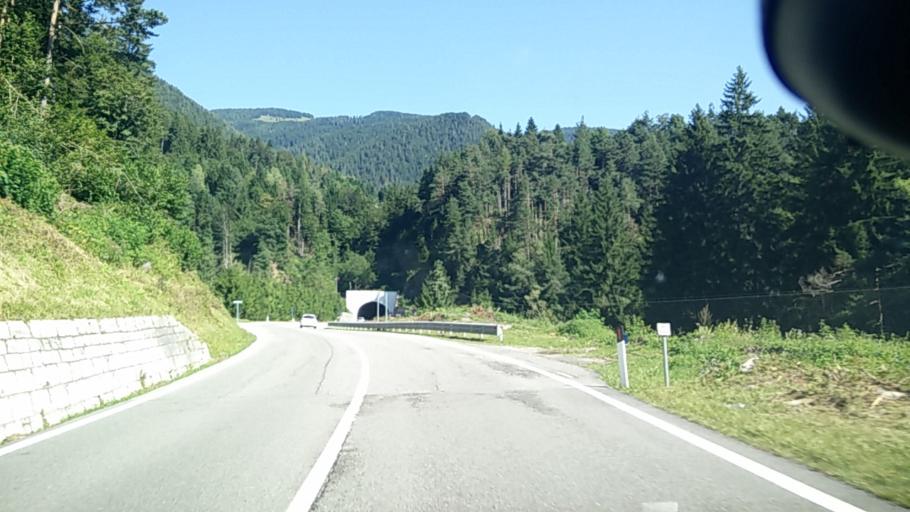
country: IT
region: Friuli Venezia Giulia
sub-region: Provincia di Udine
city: Tarvisio
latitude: 46.5140
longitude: 13.6073
